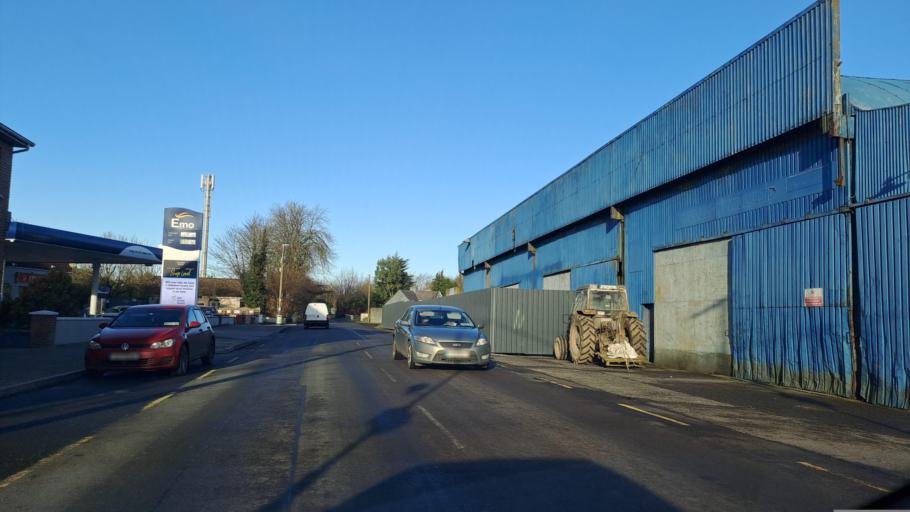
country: IE
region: Ulster
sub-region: An Cabhan
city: Mullagh
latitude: 53.8117
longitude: -6.9487
